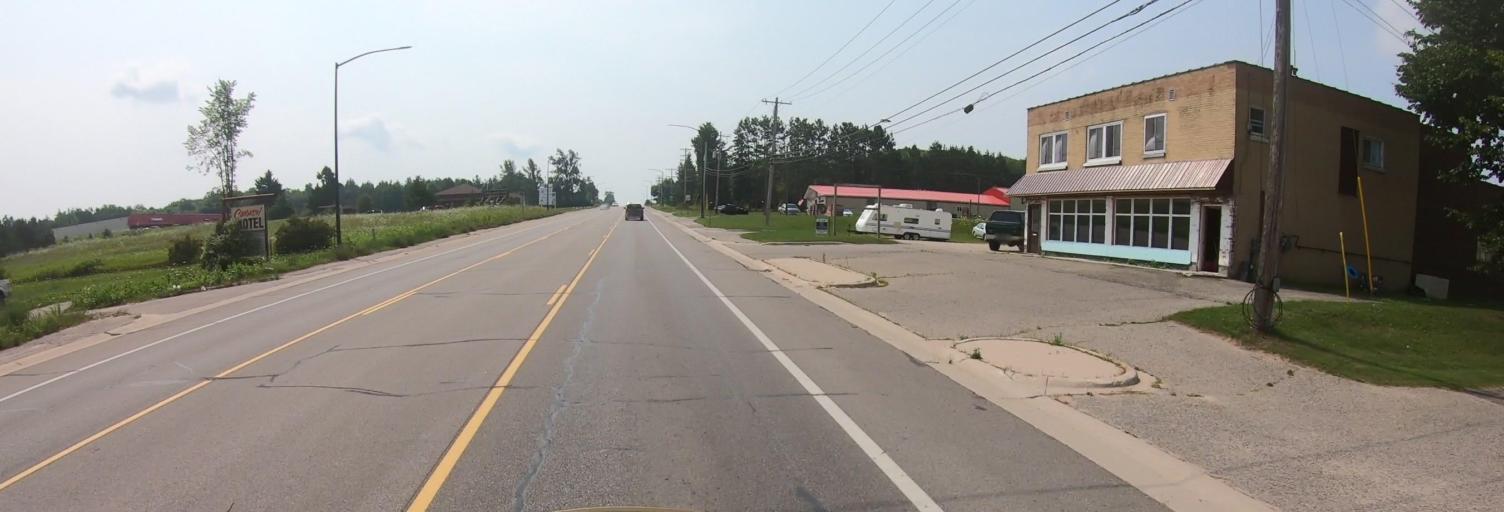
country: US
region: Michigan
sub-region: Luce County
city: Newberry
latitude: 46.3386
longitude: -85.5098
